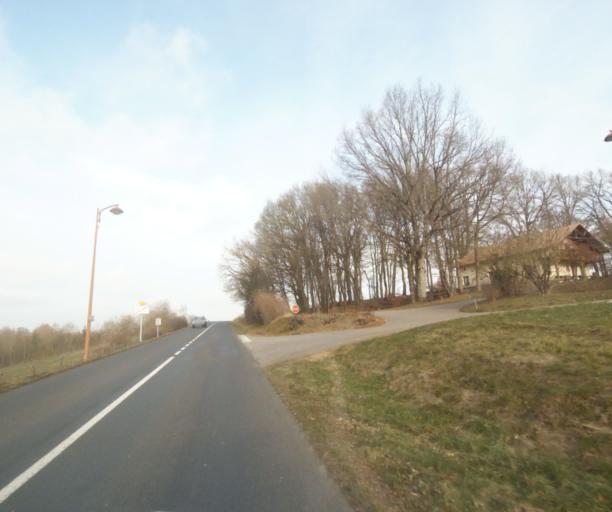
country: FR
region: Champagne-Ardenne
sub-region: Departement de la Marne
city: Sermaize-les-Bains
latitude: 48.7240
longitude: 4.9399
